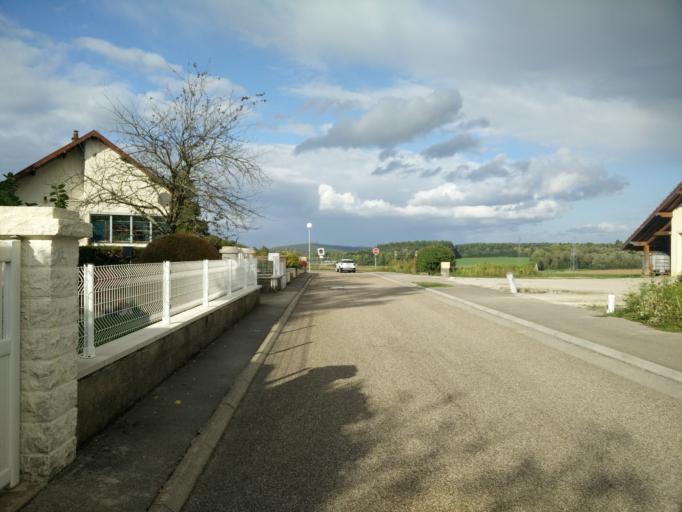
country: FR
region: Franche-Comte
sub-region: Departement du Doubs
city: Saone
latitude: 47.2260
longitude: 6.1276
